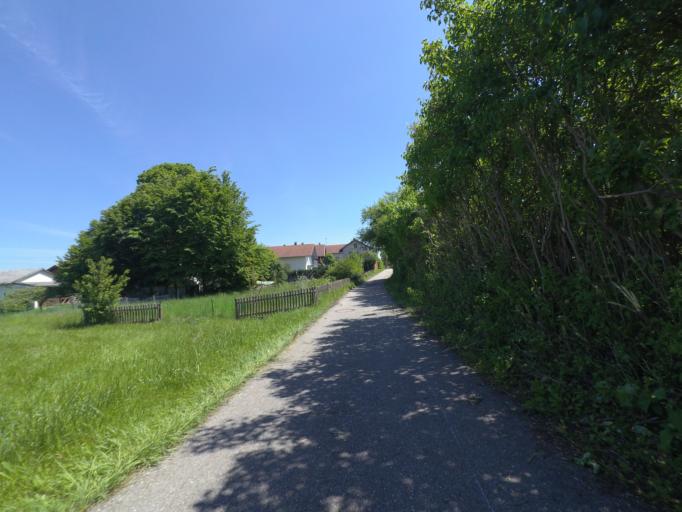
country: DE
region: Bavaria
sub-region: Upper Bavaria
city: Petting
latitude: 47.8874
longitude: 12.8460
